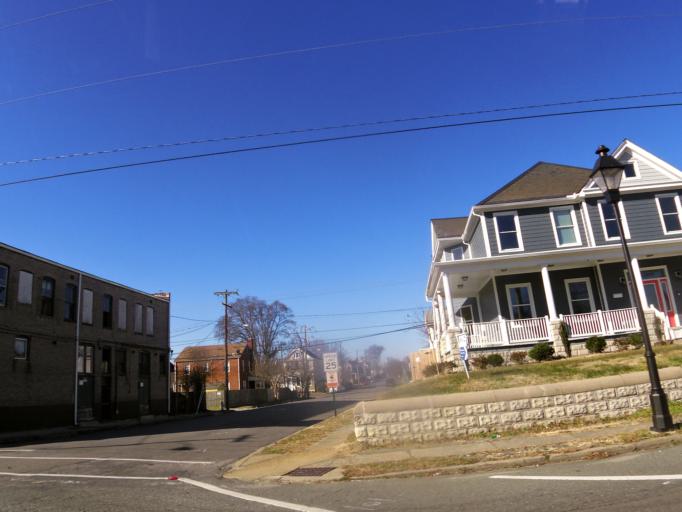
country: US
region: Virginia
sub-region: City of Richmond
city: Richmond
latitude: 37.5632
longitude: -77.4333
